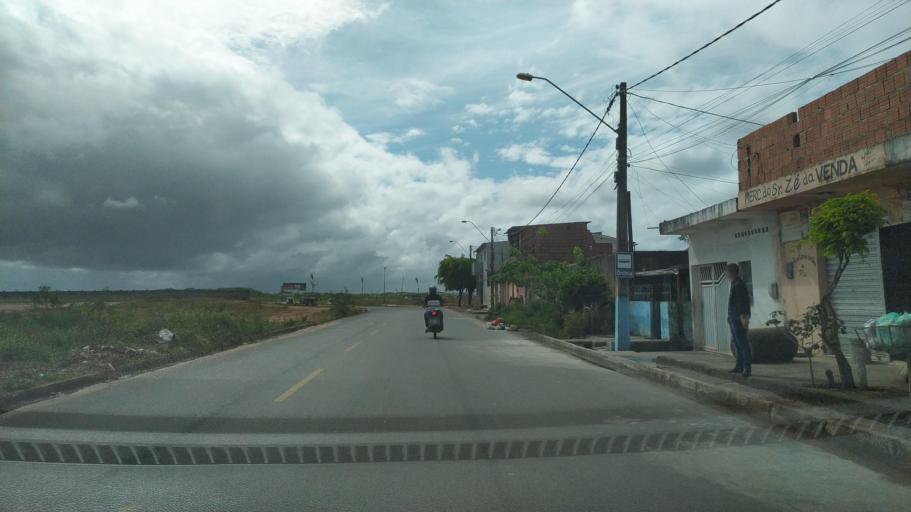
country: BR
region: Alagoas
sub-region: Satuba
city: Satuba
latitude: -9.5415
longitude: -35.7642
